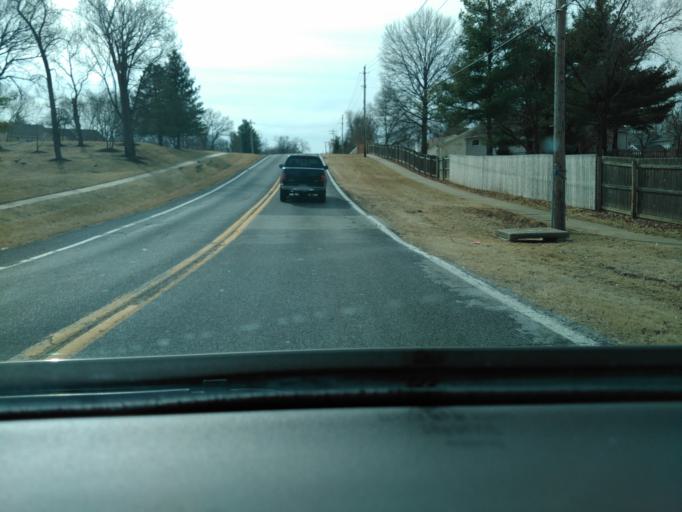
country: US
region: Missouri
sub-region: Saint Louis County
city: Valley Park
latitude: 38.5665
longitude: -90.5110
